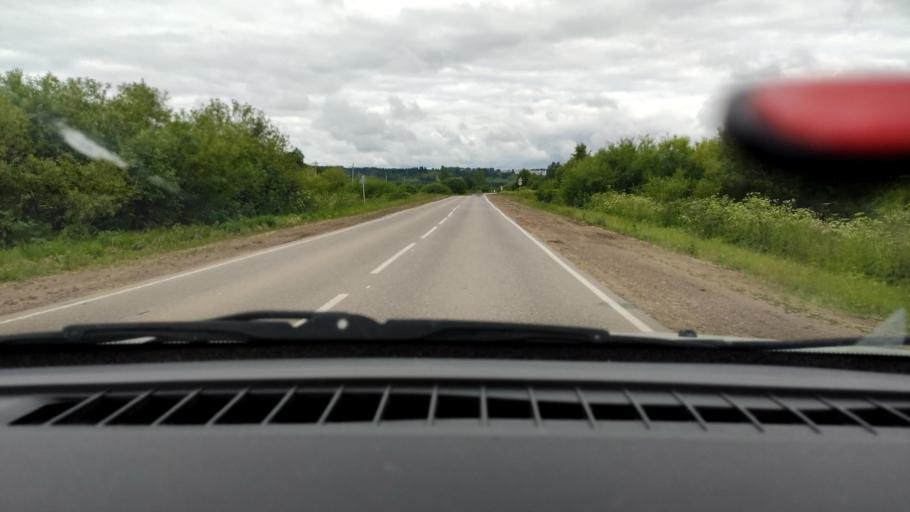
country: RU
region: Perm
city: Chaykovskaya
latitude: 58.0926
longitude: 55.6039
